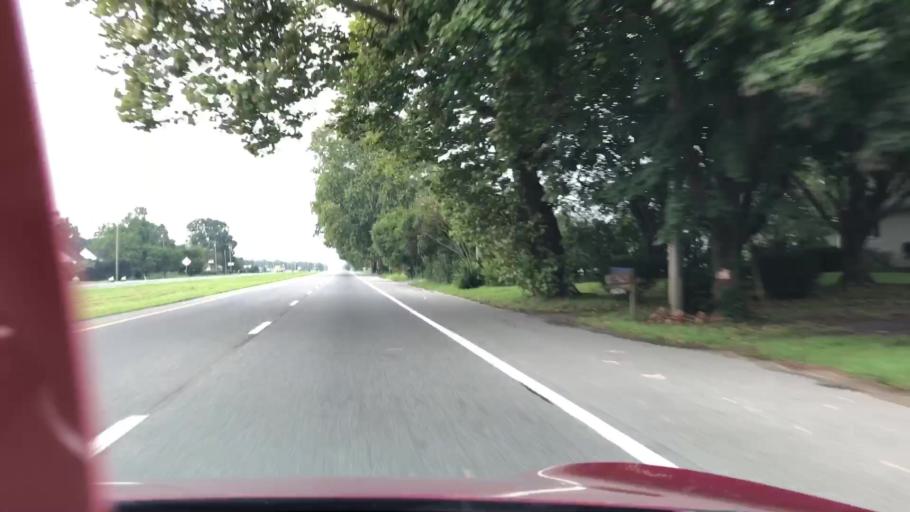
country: US
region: Delaware
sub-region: Kent County
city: Felton
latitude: 39.0331
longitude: -75.5613
